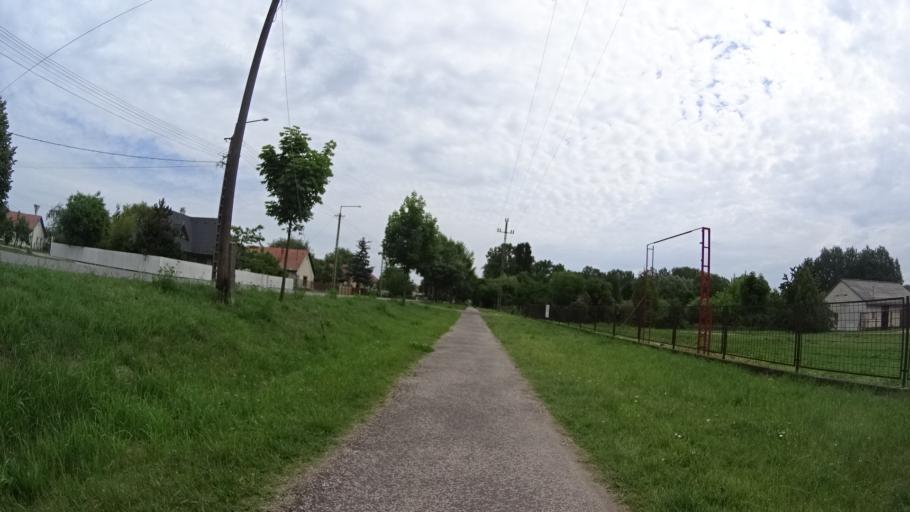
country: HU
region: Bacs-Kiskun
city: Tiszakecske
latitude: 46.9288
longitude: 20.0847
